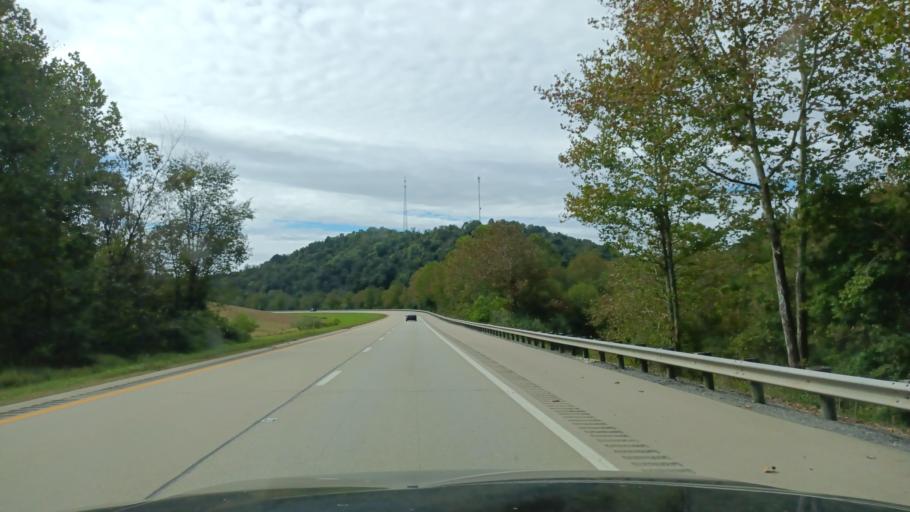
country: US
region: West Virginia
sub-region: Doddridge County
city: West Union
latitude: 39.2986
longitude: -80.7544
